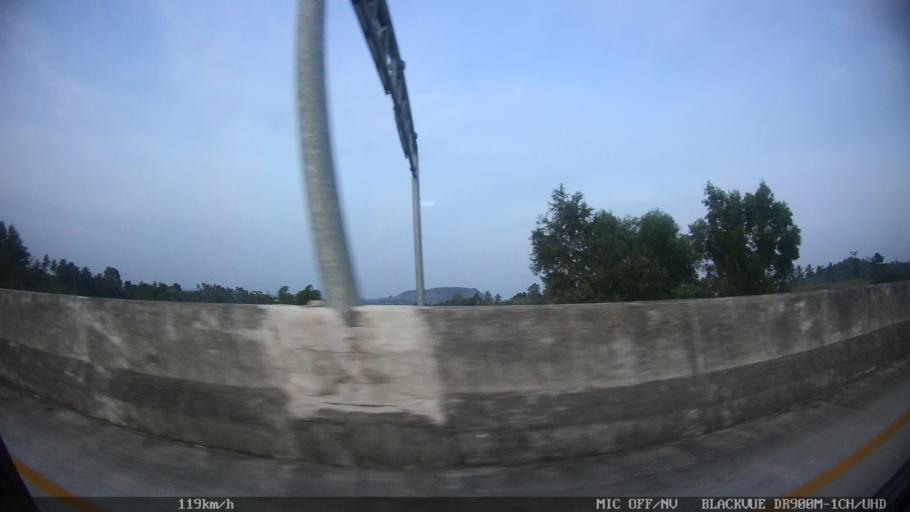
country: ID
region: Lampung
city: Penengahan
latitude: -5.8005
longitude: 105.7298
